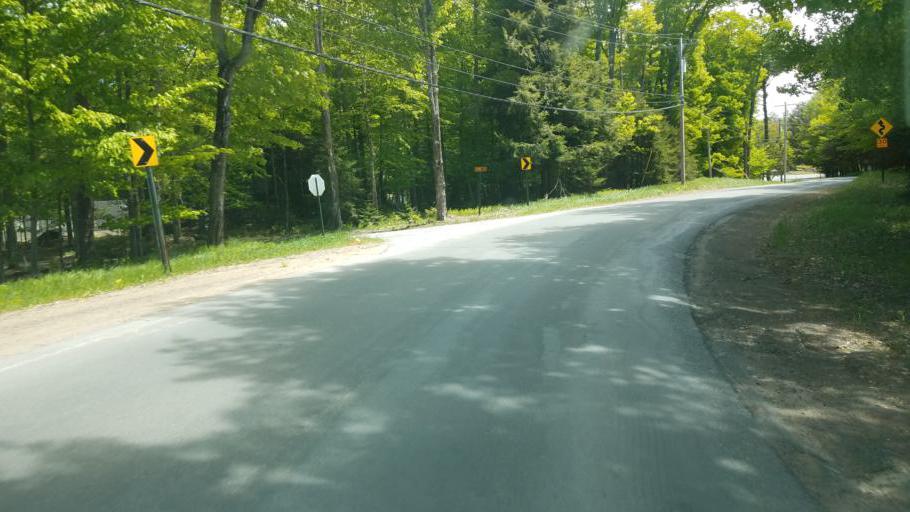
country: US
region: New York
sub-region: Oneida County
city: Boonville
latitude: 43.7125
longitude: -74.9468
